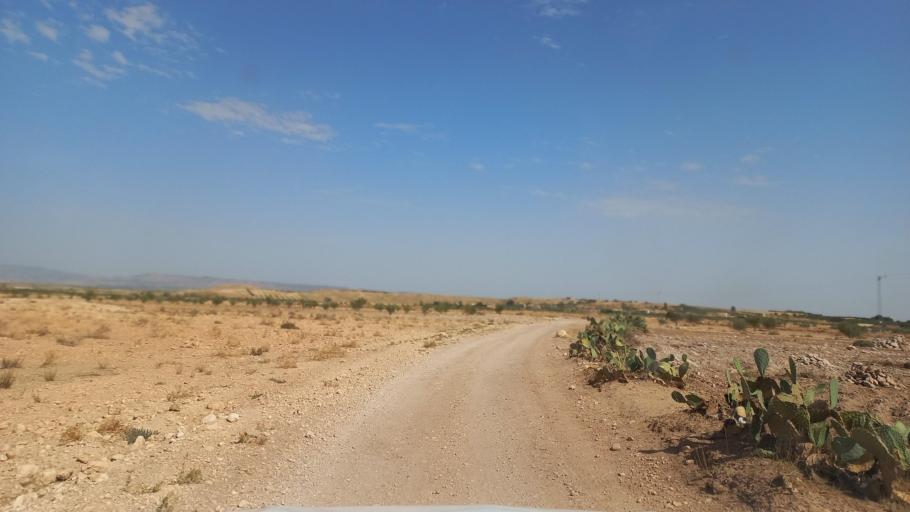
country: TN
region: Al Qasrayn
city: Kasserine
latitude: 35.2797
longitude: 8.9607
